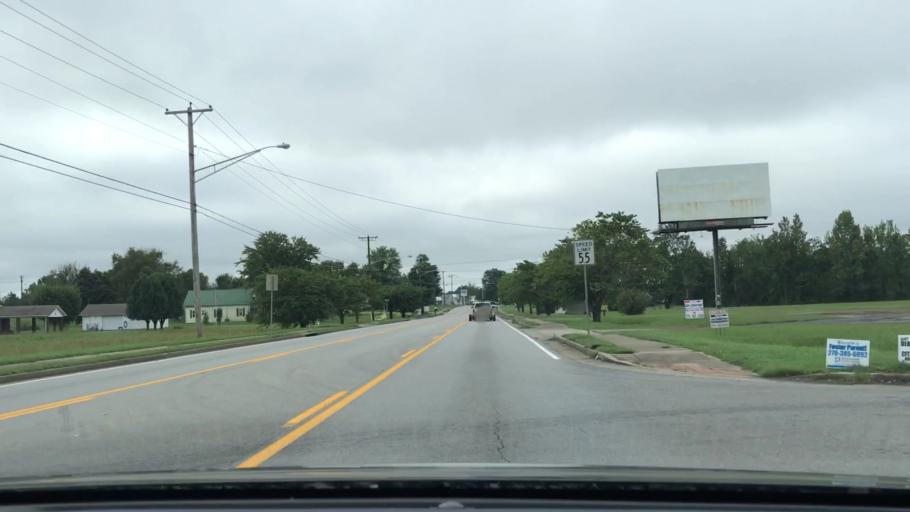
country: US
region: Kentucky
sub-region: Russell County
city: Russell Springs
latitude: 37.0245
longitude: -85.0769
